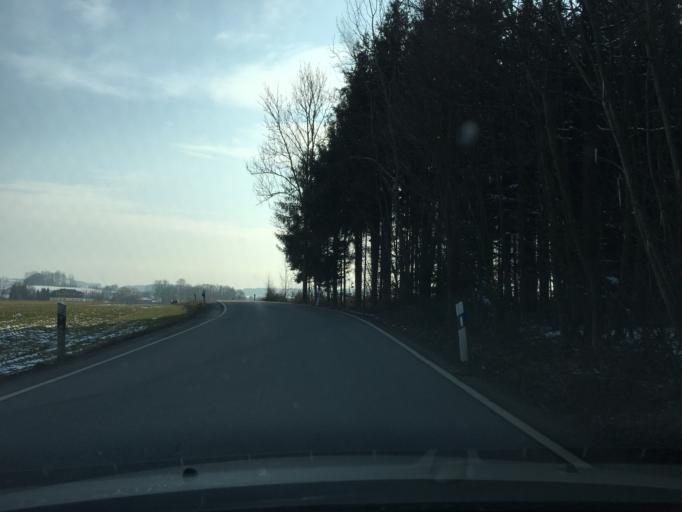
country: DE
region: Bavaria
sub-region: Lower Bavaria
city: Gangkofen
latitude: 48.3895
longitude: 12.5500
